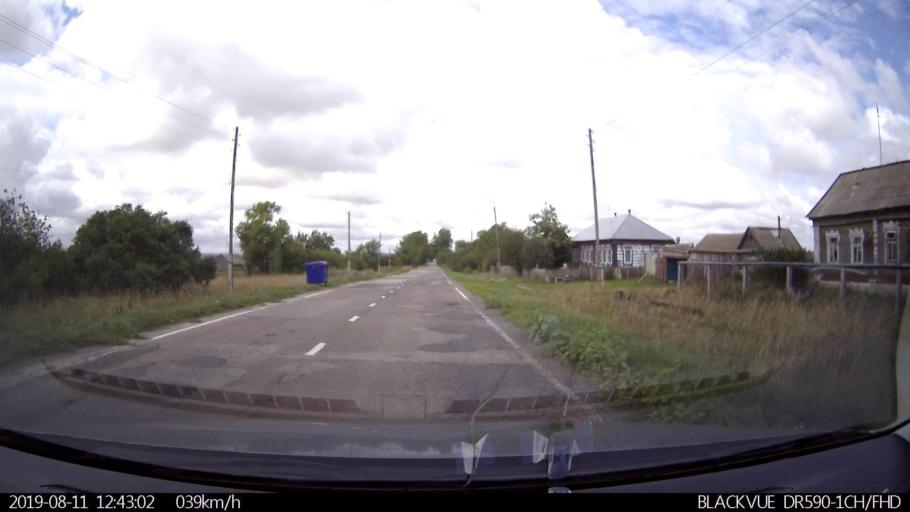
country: RU
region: Ulyanovsk
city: Ignatovka
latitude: 53.8493
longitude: 47.7456
